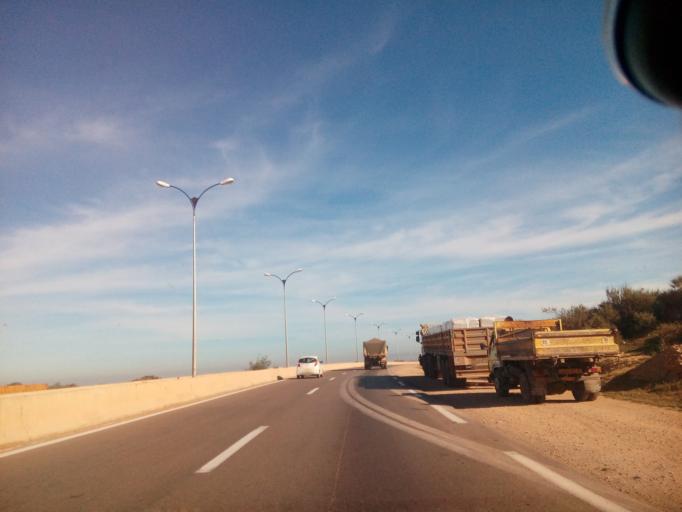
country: DZ
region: Oran
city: Ain el Bya
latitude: 35.7941
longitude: -0.0919
